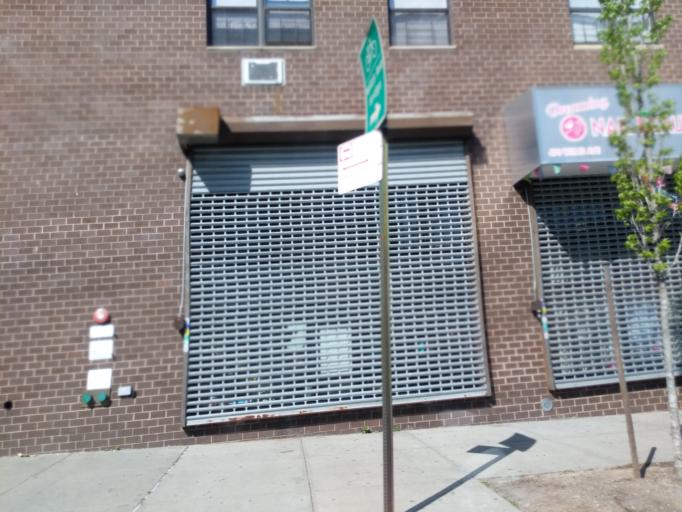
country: US
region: New York
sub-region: New York County
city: Inwood
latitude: 40.8142
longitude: -73.9195
